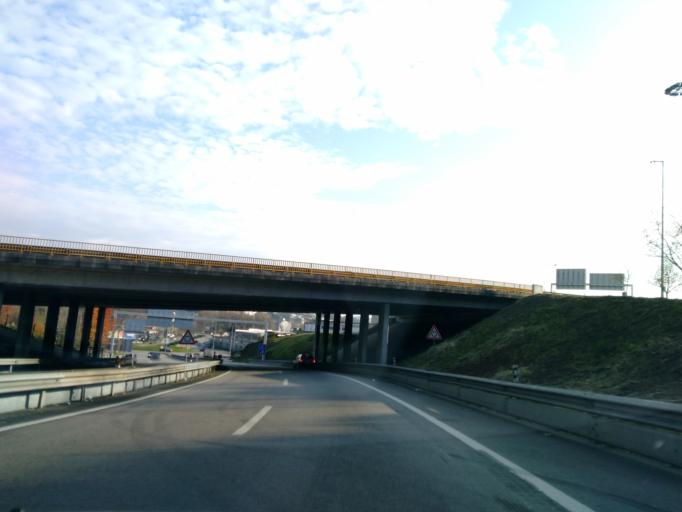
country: PT
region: Porto
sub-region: Gondomar
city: Valbom
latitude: 41.1473
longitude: -8.5812
